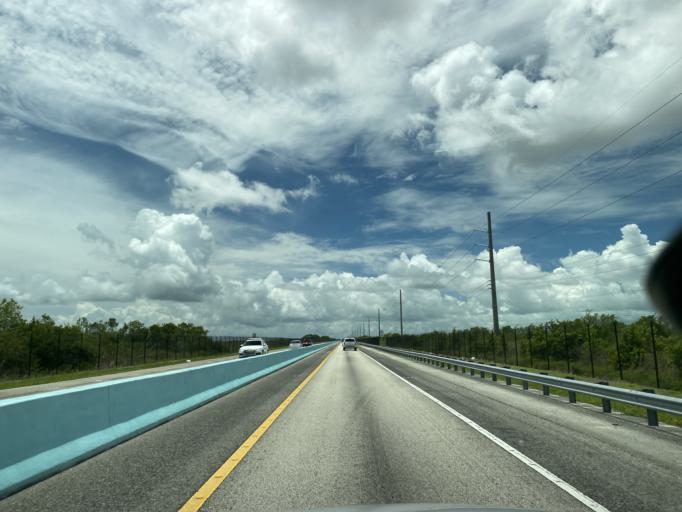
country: US
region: Florida
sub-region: Miami-Dade County
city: Florida City
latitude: 25.3627
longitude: -80.4608
